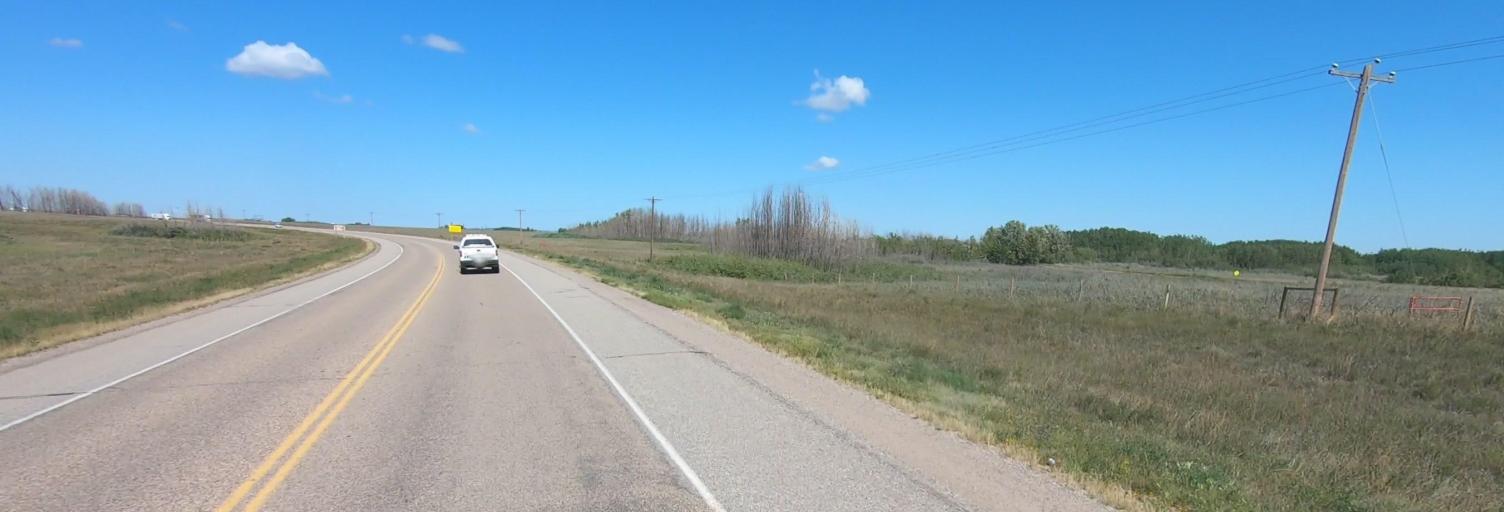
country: CA
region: Alberta
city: Strathmore
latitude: 50.8788
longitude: -113.1683
